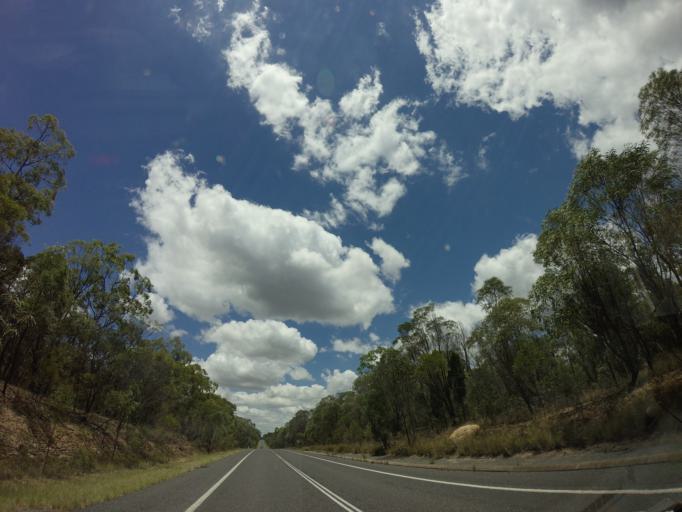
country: AU
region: Queensland
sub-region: Western Downs
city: Dalby
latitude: -27.9704
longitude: 151.0353
